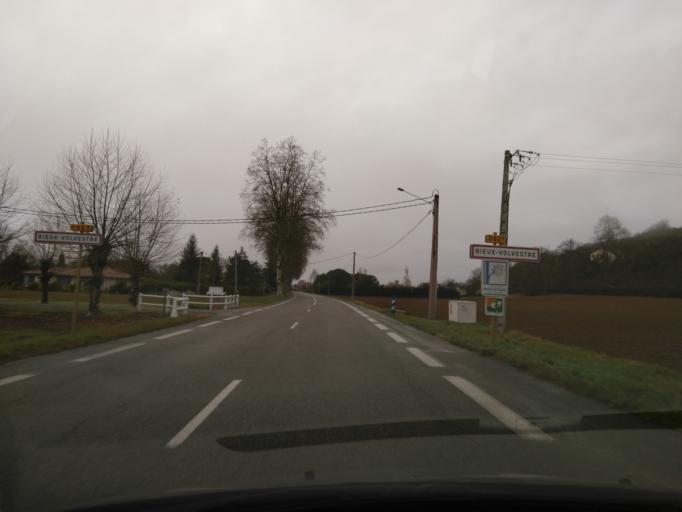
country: FR
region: Midi-Pyrenees
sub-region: Departement de la Haute-Garonne
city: Rieux-Volvestre
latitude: 43.2485
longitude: 1.2022
